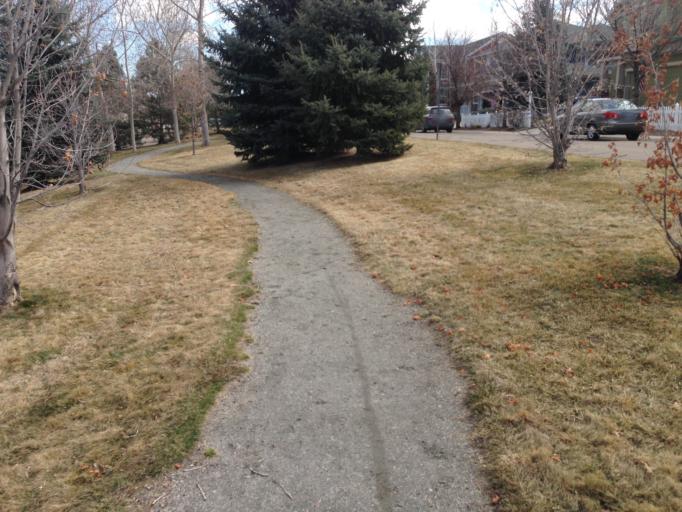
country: US
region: Colorado
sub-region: Boulder County
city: Louisville
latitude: 40.0059
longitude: -105.1340
